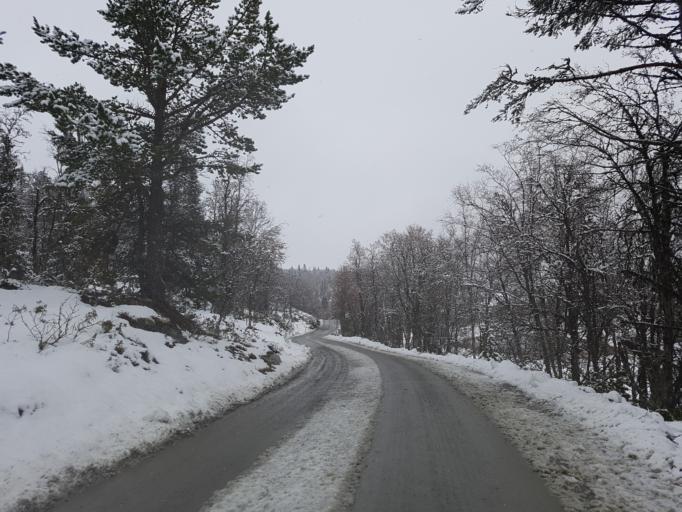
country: NO
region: Oppland
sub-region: Sel
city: Otta
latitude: 61.8024
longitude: 9.7024
